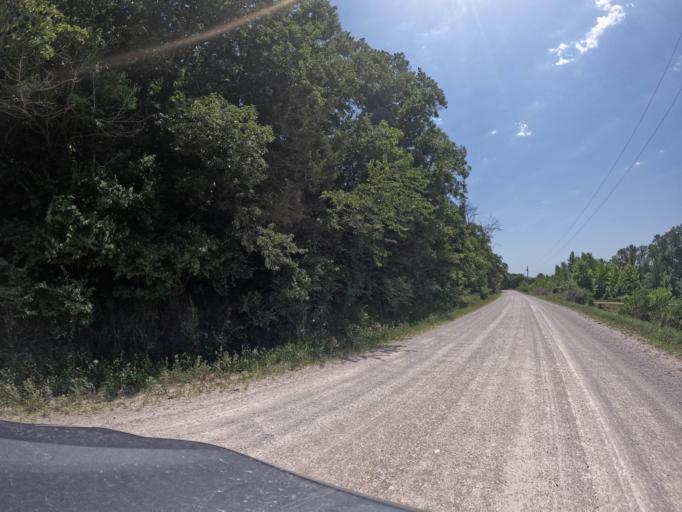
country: US
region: Iowa
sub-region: Henry County
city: Mount Pleasant
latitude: 40.8965
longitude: -91.5497
